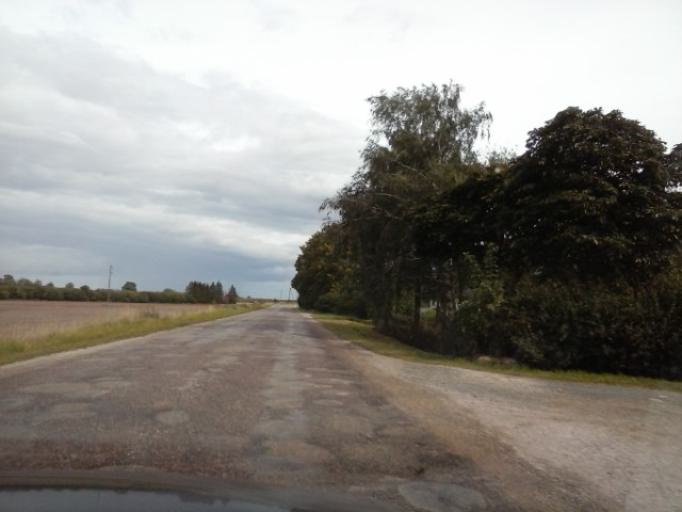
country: LV
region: Tukuma Rajons
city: Tukums
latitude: 56.9230
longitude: 23.2342
